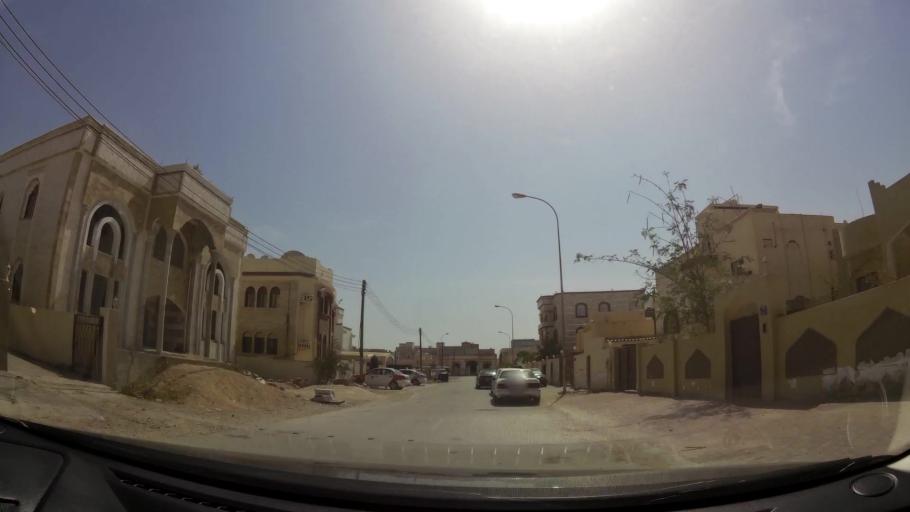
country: OM
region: Zufar
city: Salalah
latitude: 17.0472
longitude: 54.1590
